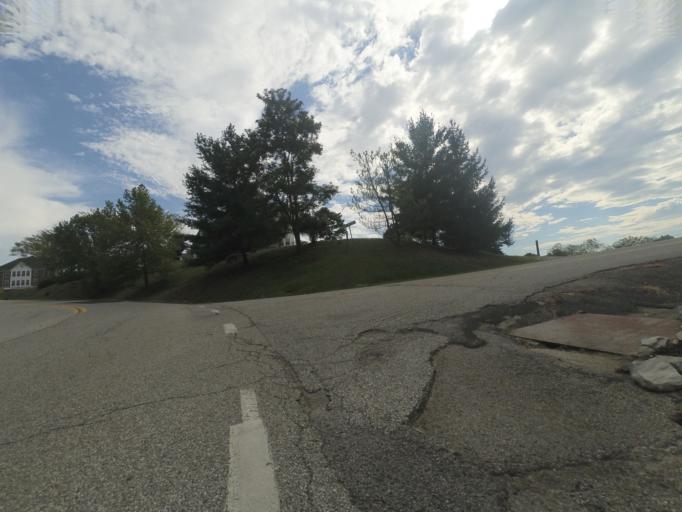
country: US
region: West Virginia
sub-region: Cabell County
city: Huntington
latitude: 38.3924
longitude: -82.4620
